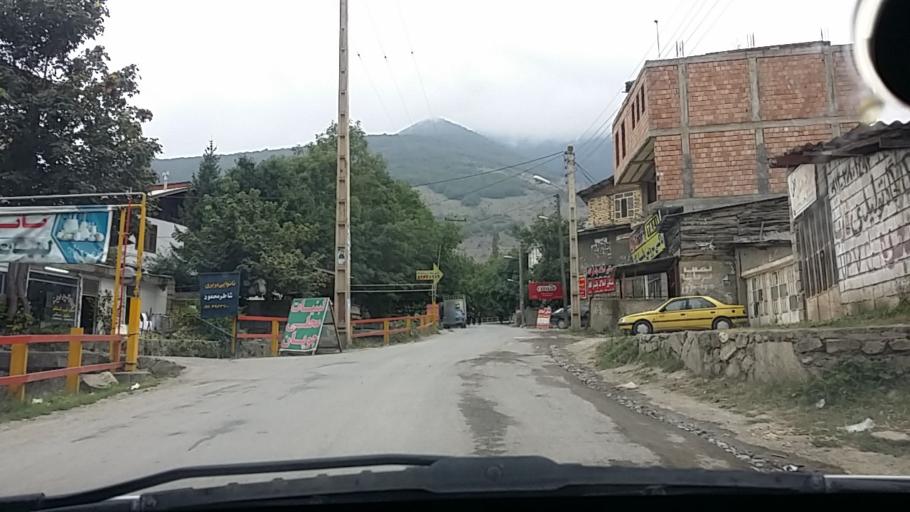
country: IR
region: Mazandaran
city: `Abbasabad
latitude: 36.4845
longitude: 51.1349
